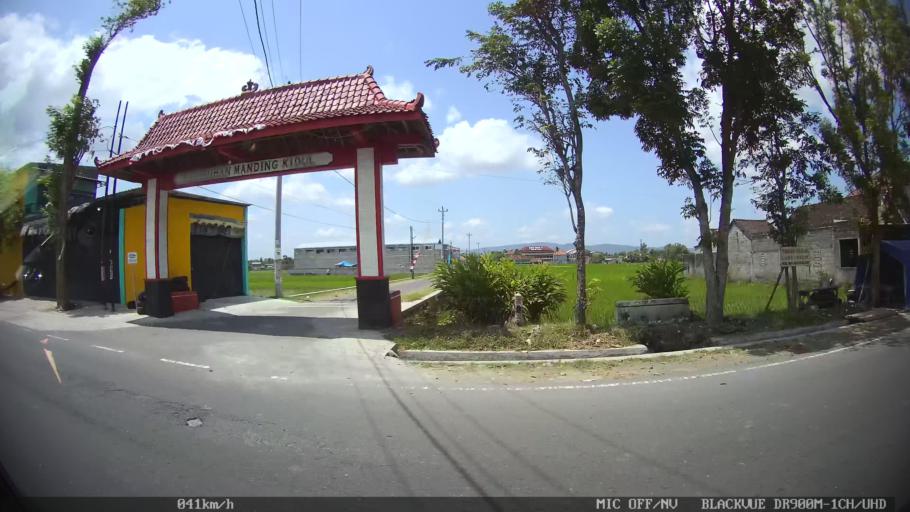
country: ID
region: Daerah Istimewa Yogyakarta
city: Bantul
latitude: -7.9017
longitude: 110.3458
